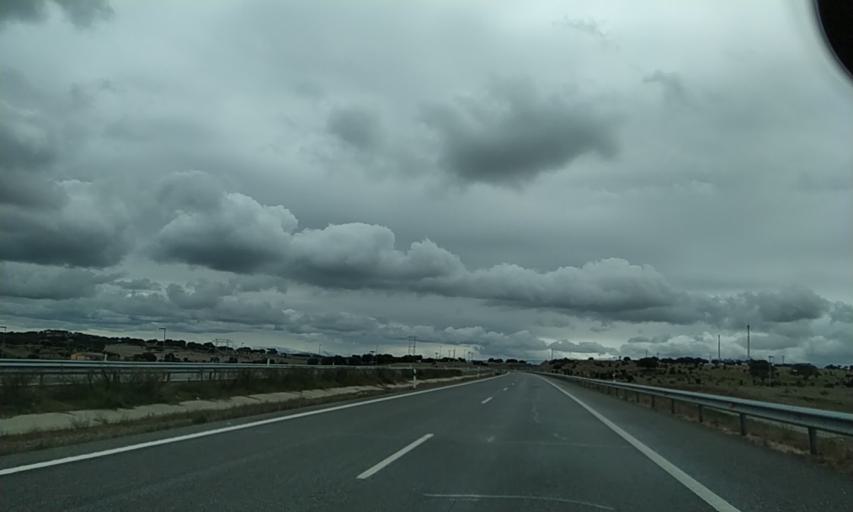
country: ES
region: Castille and Leon
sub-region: Provincia de Salamanca
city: Montejo
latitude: 40.6323
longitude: -5.6320
